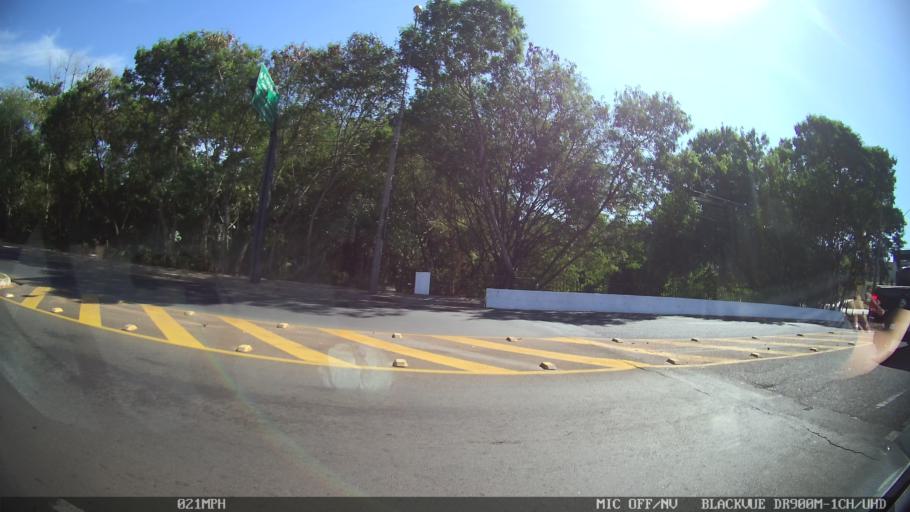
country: BR
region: Sao Paulo
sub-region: Sao Jose Do Rio Preto
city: Sao Jose do Rio Preto
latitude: -20.7829
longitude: -49.3802
